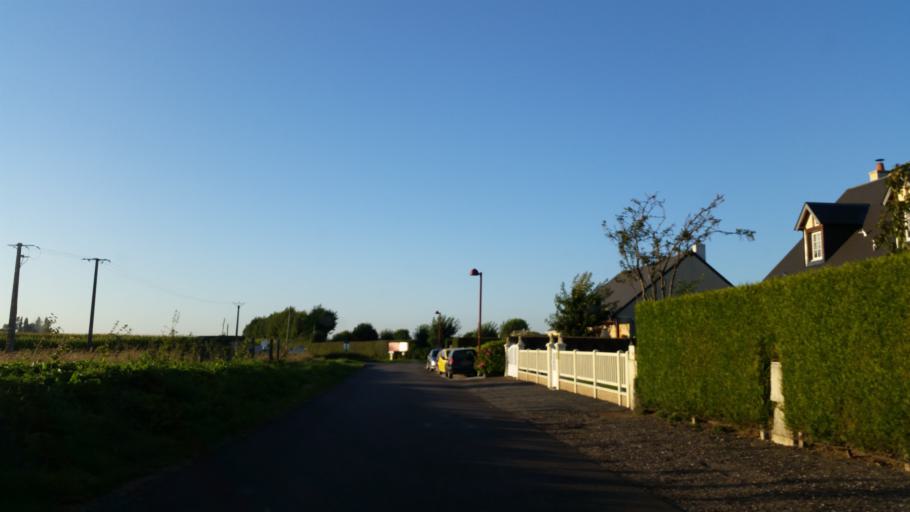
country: FR
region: Lower Normandy
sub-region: Departement du Calvados
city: Equemauville
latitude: 49.3963
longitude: 0.2056
